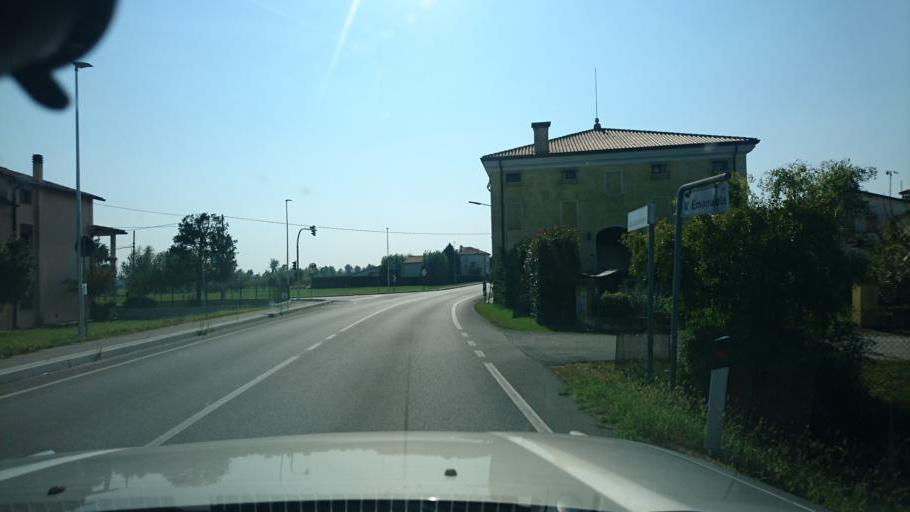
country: IT
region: Veneto
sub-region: Provincia di Padova
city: Gazzo
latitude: 45.5698
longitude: 11.7108
